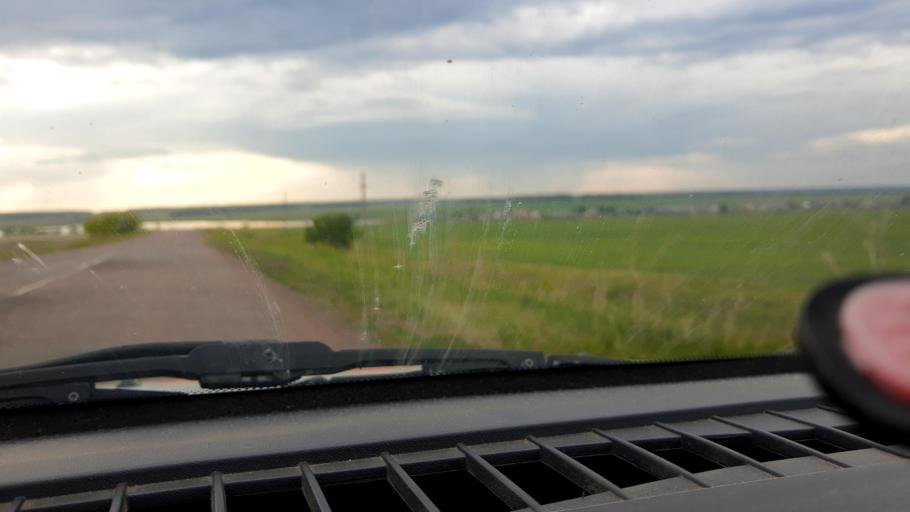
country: RU
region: Bashkortostan
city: Asanovo
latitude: 54.8469
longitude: 55.6040
